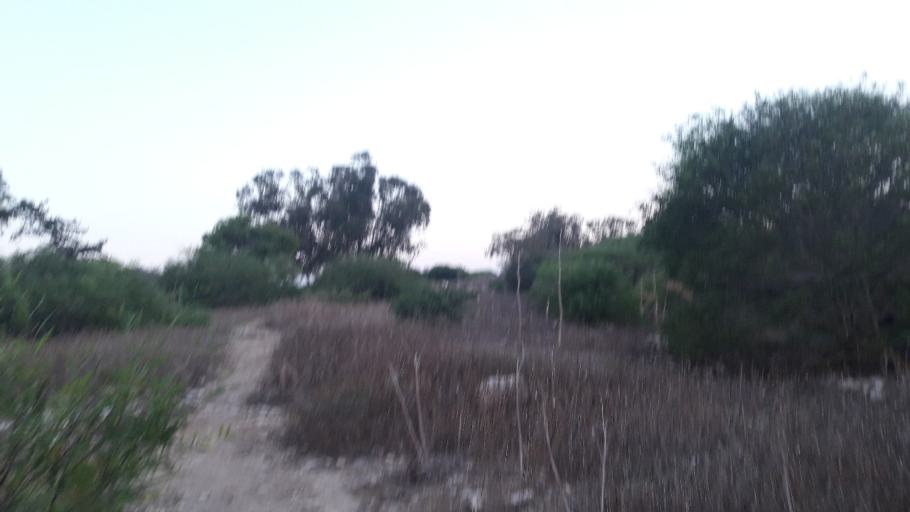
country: CY
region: Ammochostos
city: Famagusta
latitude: 35.1820
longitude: 33.9013
